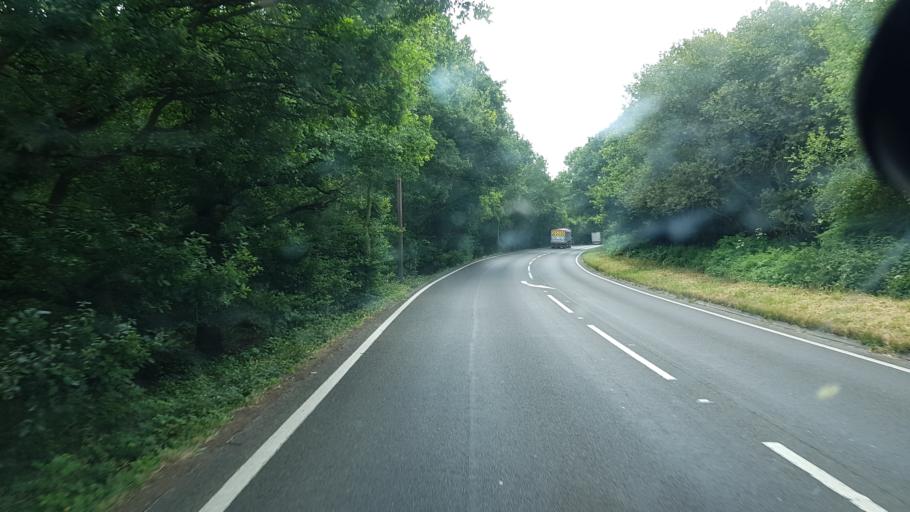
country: GB
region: England
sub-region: Surrey
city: Felbridge
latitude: 51.1685
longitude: -0.0501
